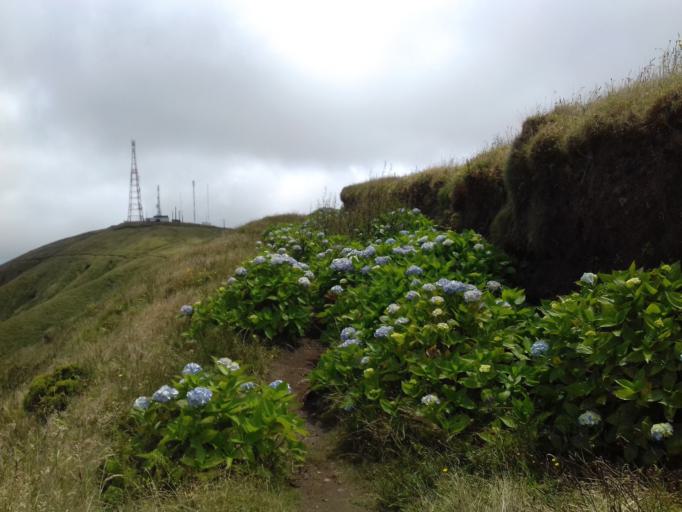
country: PT
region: Azores
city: Ribeira Grande
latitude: 38.5776
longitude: -28.7204
